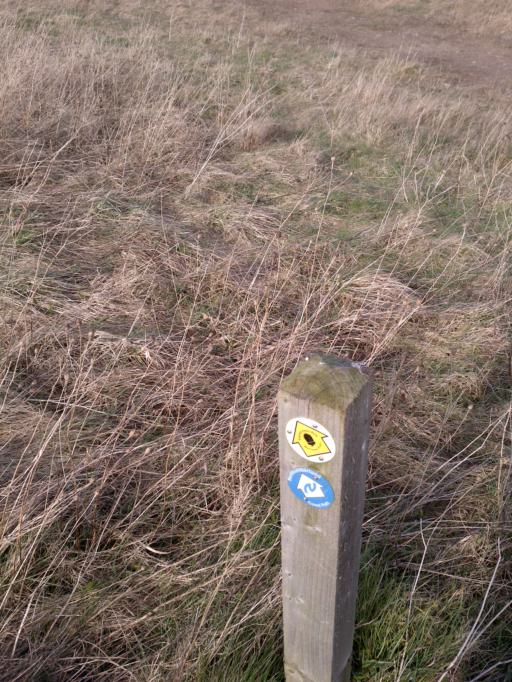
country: GB
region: England
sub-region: Northumberland
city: Lynemouth
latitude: 55.2106
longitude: -1.5256
